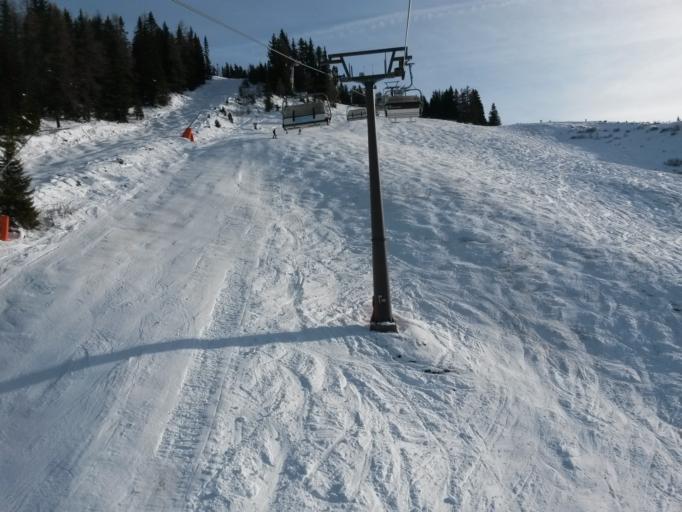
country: AT
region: Salzburg
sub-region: Politischer Bezirk Sankt Johann im Pongau
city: Dorfgastein
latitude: 47.2363
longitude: 13.1330
